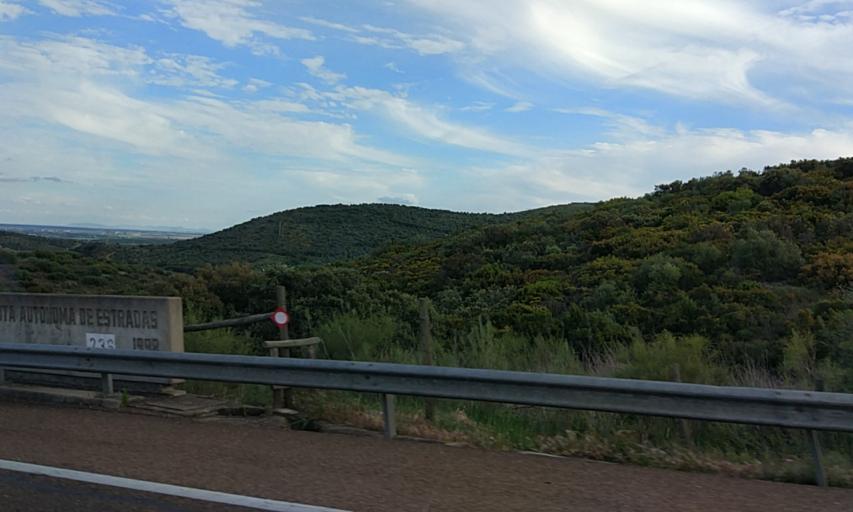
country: PT
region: Portalegre
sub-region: Elvas
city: Elvas
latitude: 38.9089
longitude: -7.1715
